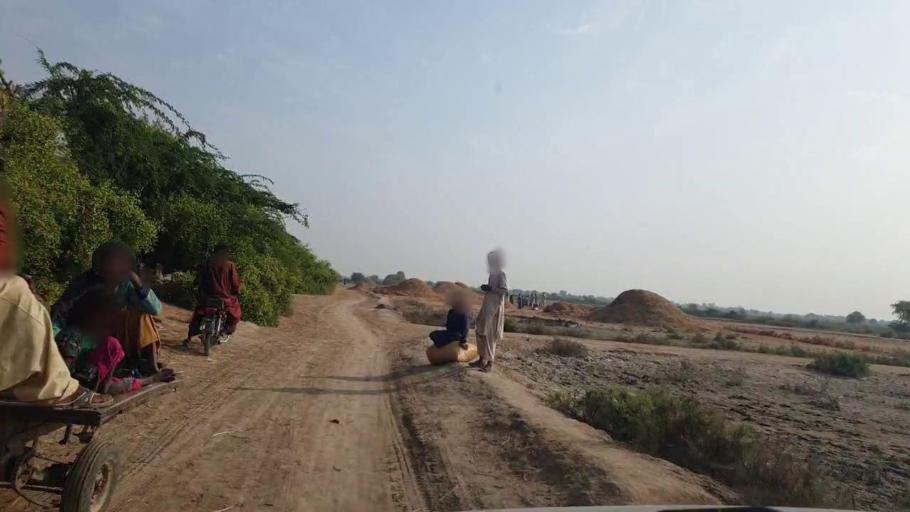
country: PK
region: Sindh
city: Talhar
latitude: 24.8975
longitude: 68.8888
